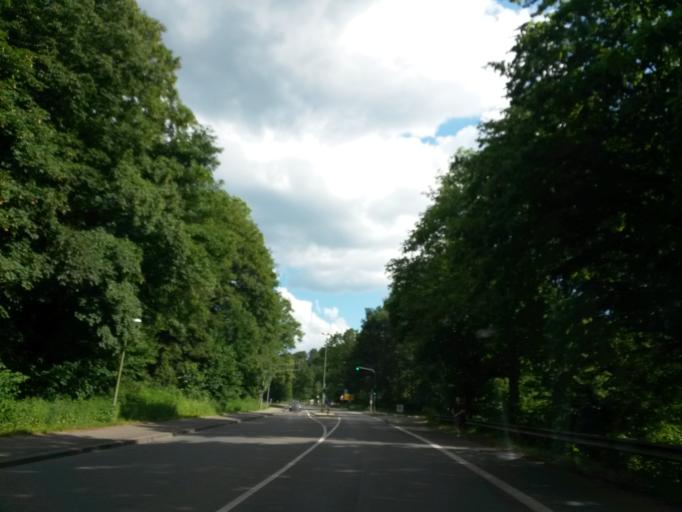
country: DE
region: North Rhine-Westphalia
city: Lohmar
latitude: 50.8468
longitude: 7.2256
